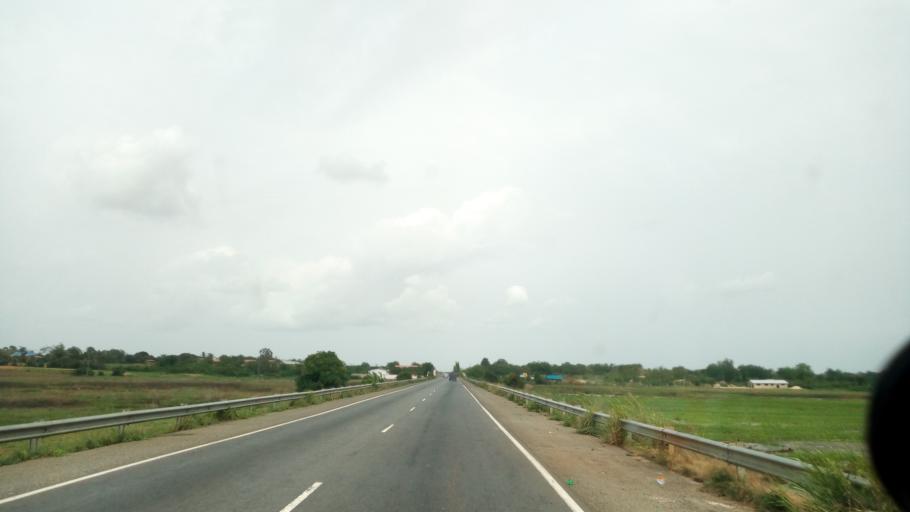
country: GH
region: Volta
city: Keta
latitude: 6.0608
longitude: 0.9384
